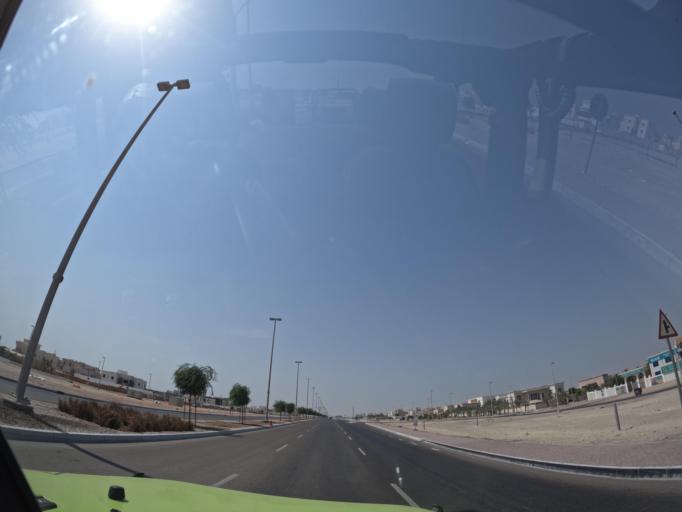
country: AE
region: Abu Dhabi
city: Abu Dhabi
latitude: 24.3507
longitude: 54.6220
